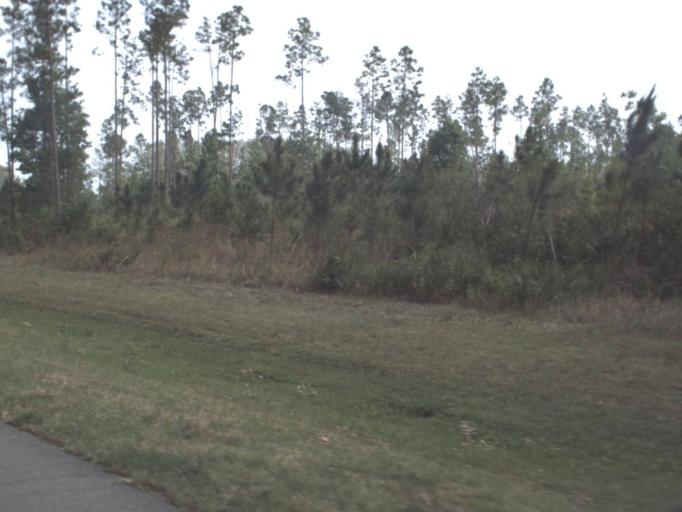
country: US
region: Florida
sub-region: Flagler County
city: Bunnell
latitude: 29.4722
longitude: -81.3236
